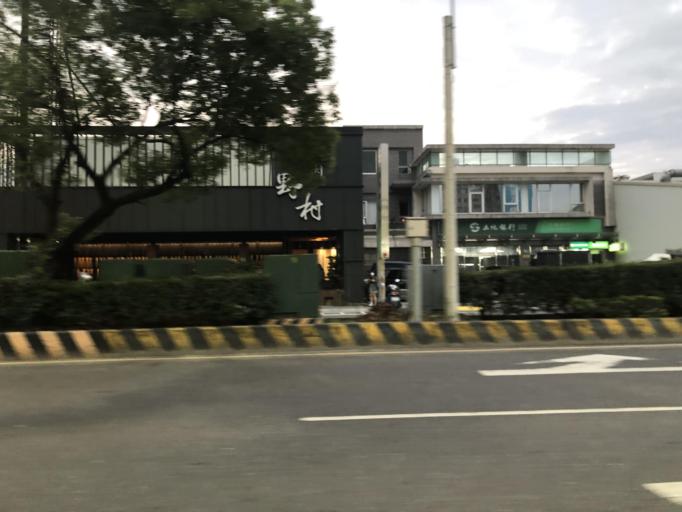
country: TW
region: Taiwan
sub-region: Tainan
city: Tainan
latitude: 23.0182
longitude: 120.2625
